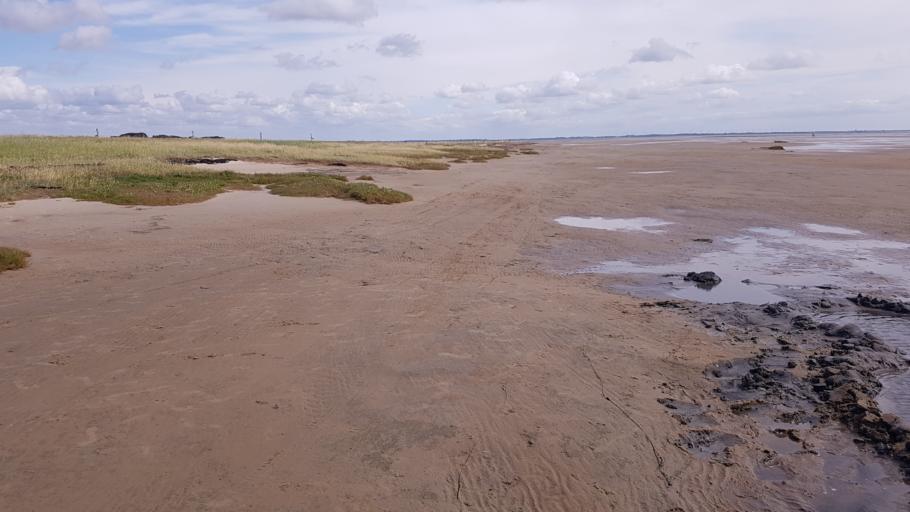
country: DE
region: Schleswig-Holstein
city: List
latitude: 55.0756
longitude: 8.5352
